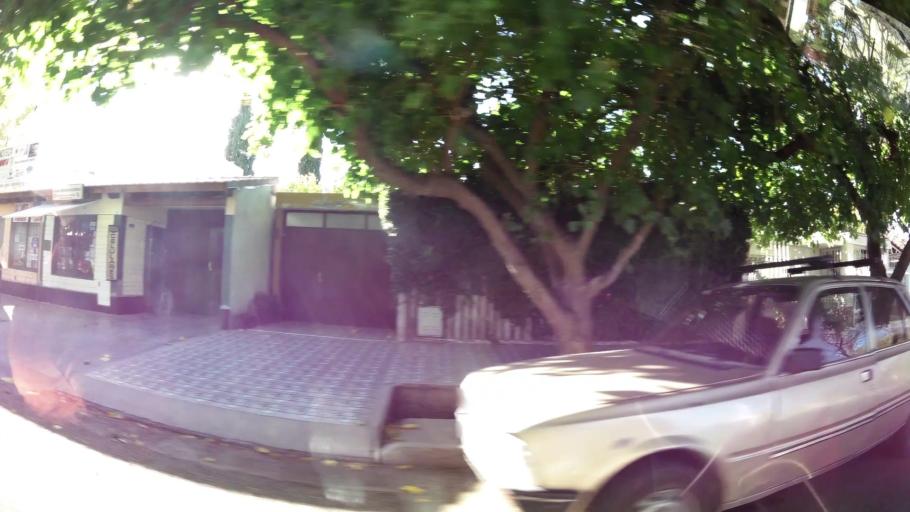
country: AR
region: Mendoza
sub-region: Departamento de Godoy Cruz
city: Godoy Cruz
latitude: -32.9370
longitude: -68.8331
